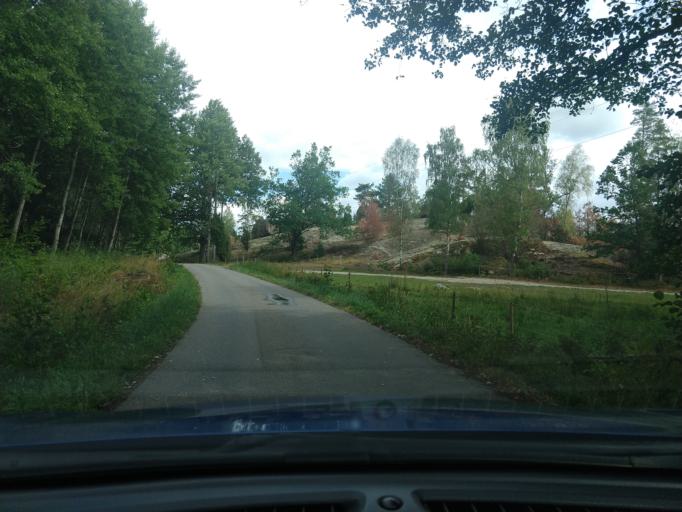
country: SE
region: Blekinge
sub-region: Ronneby Kommun
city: Brakne-Hoby
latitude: 56.2876
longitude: 15.1921
